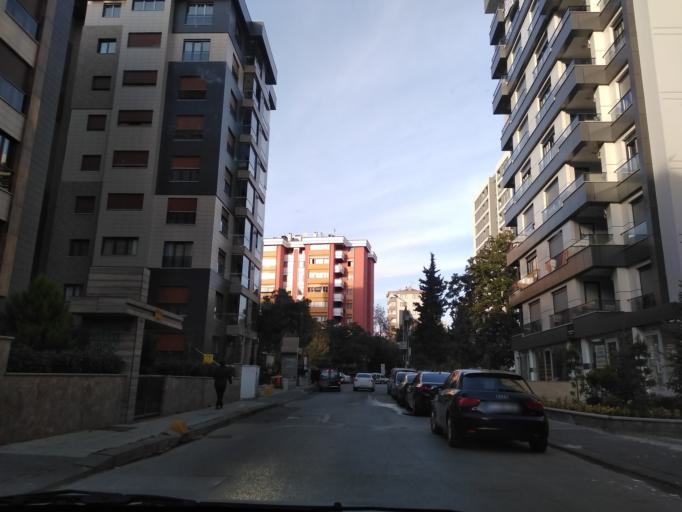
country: TR
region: Istanbul
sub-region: Atasehir
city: Atasehir
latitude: 40.9731
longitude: 29.0923
